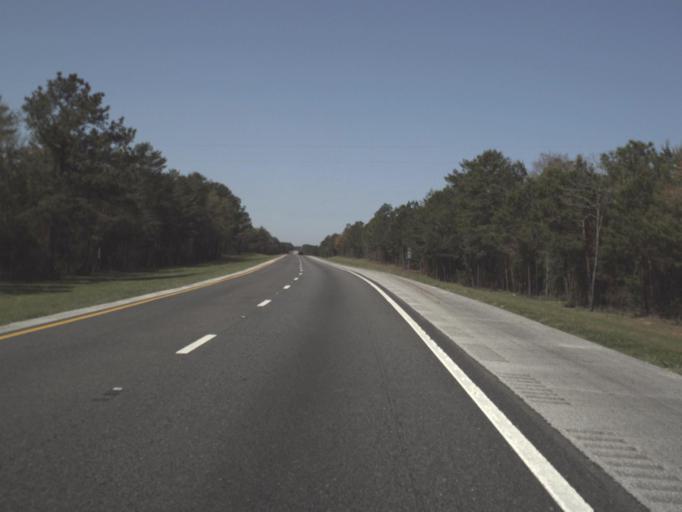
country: US
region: Florida
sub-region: Okaloosa County
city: Crestview
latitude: 30.7339
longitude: -86.3750
